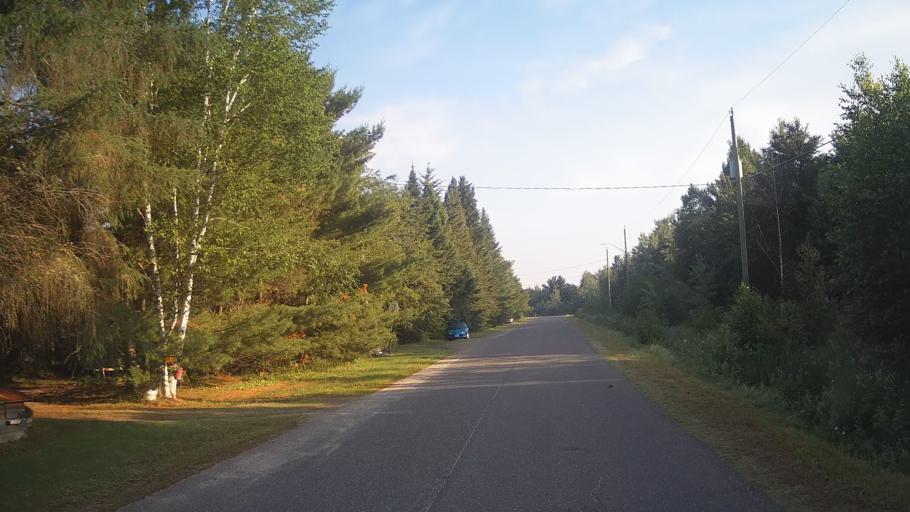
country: CA
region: Ontario
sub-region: Rainy River District
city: Atikokan
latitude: 49.4025
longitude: -91.6657
